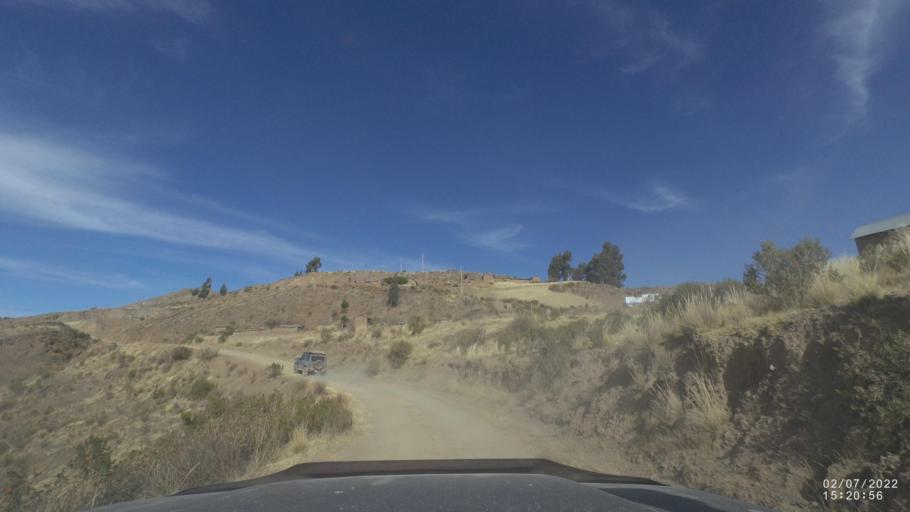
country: BO
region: Cochabamba
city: Irpa Irpa
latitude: -17.8715
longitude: -66.4252
